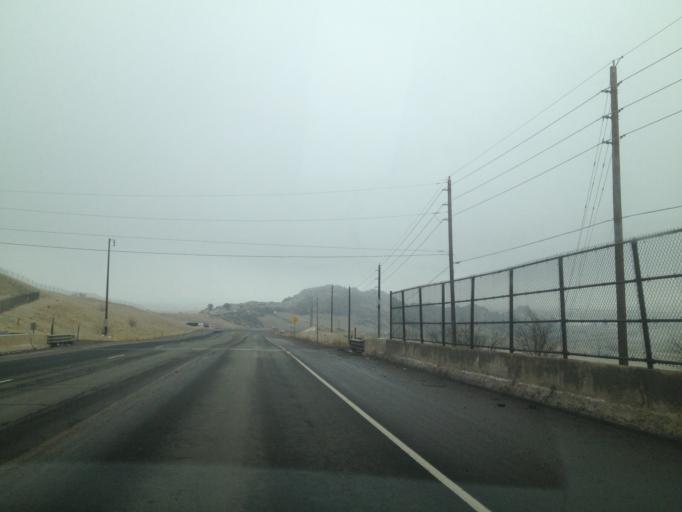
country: US
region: Colorado
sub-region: Jefferson County
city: Golden
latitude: 39.8593
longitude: -105.2349
